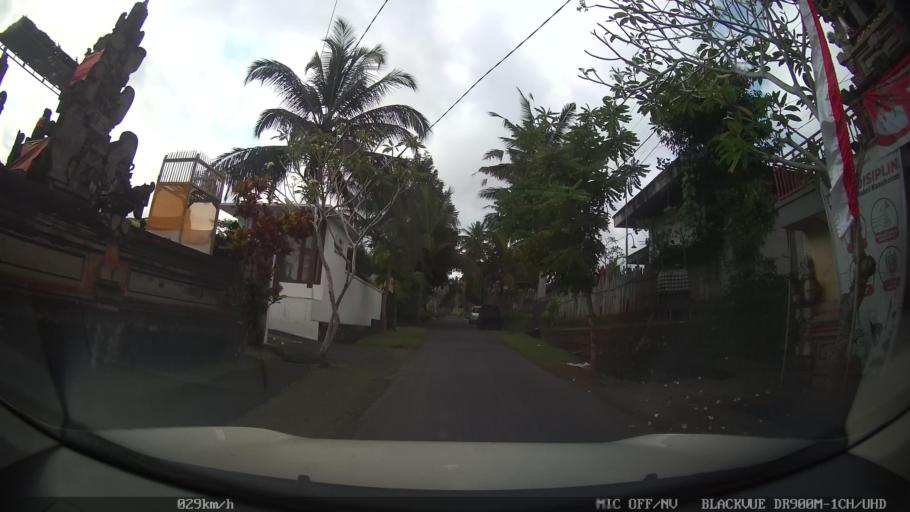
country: ID
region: Bali
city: Banjar Pesalakan
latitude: -8.5031
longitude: 115.3038
